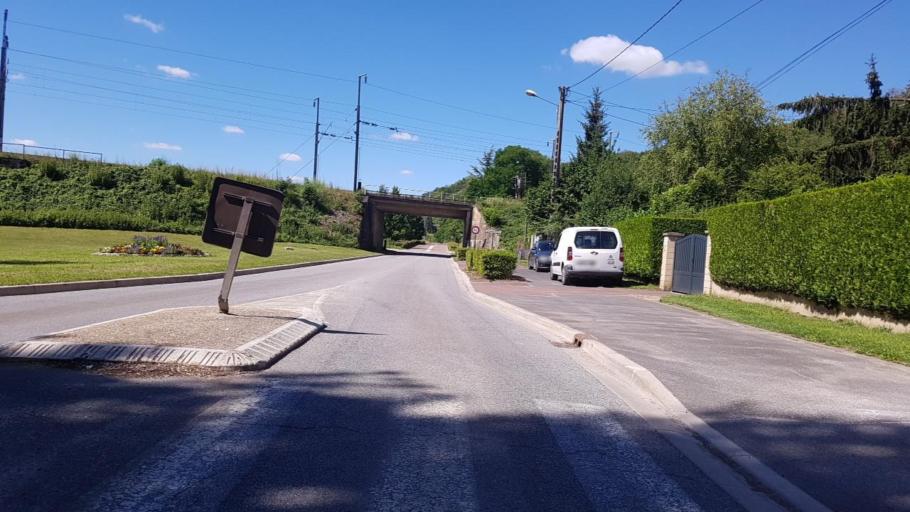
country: FR
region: Ile-de-France
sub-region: Departement de Seine-et-Marne
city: Saacy-sur-Marne
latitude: 48.9754
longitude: 3.2148
